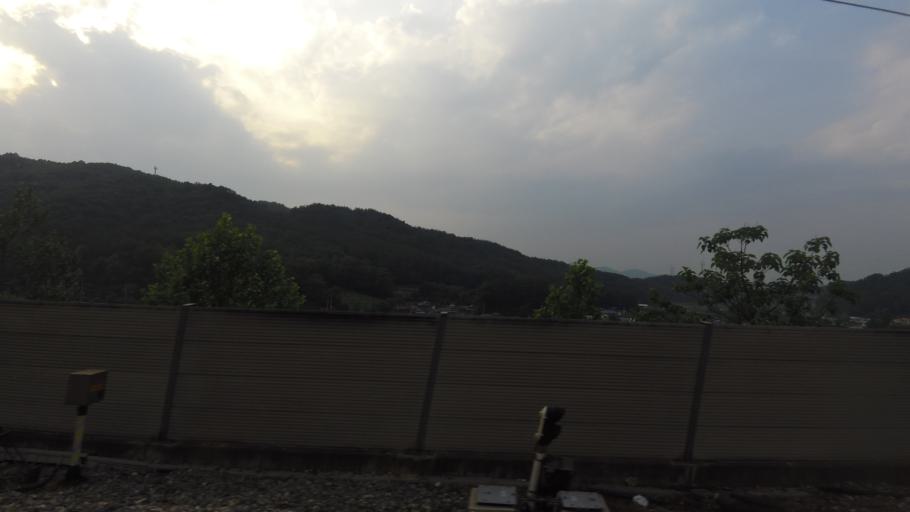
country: KR
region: Daejeon
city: Daejeon
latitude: 36.3375
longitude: 127.4921
